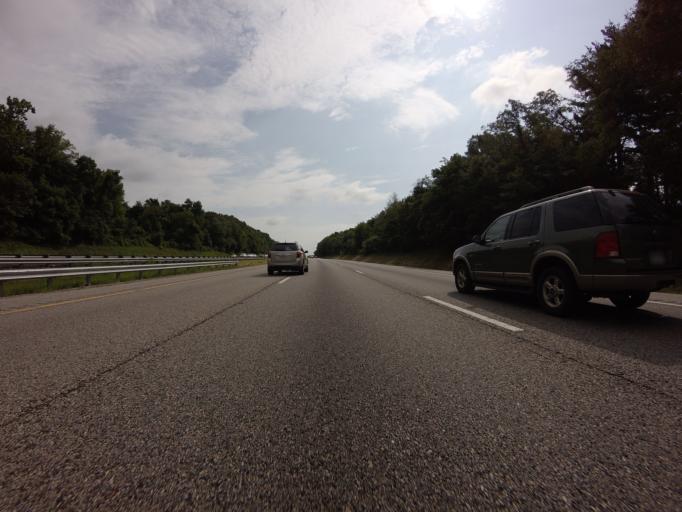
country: US
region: Maryland
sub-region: Cecil County
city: Elkton
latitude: 39.6421
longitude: -75.8631
